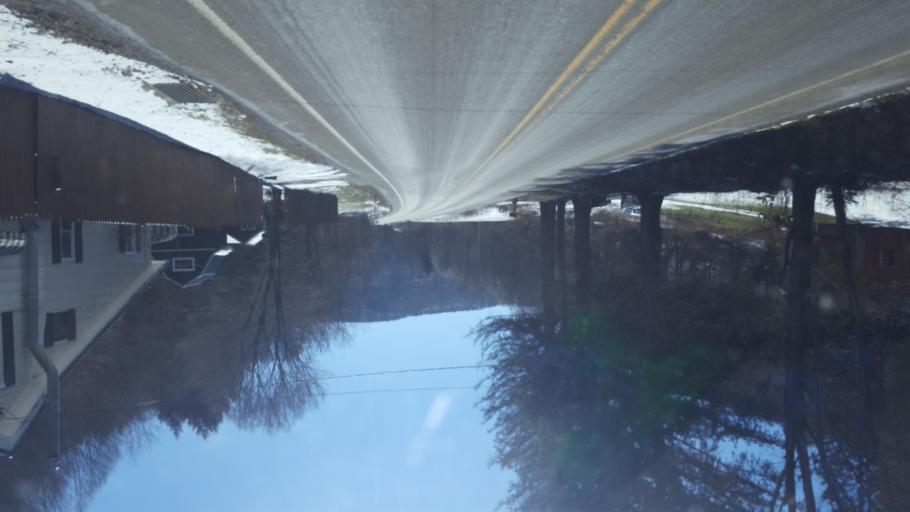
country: US
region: New York
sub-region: Allegany County
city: Andover
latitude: 42.0431
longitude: -77.7869
